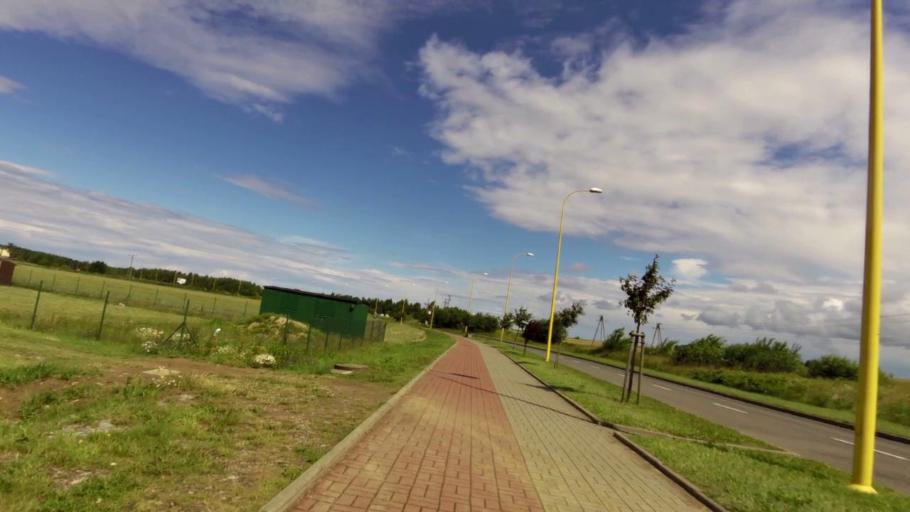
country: PL
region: West Pomeranian Voivodeship
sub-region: Powiat slawienski
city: Darlowo
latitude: 54.4411
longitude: 16.4067
